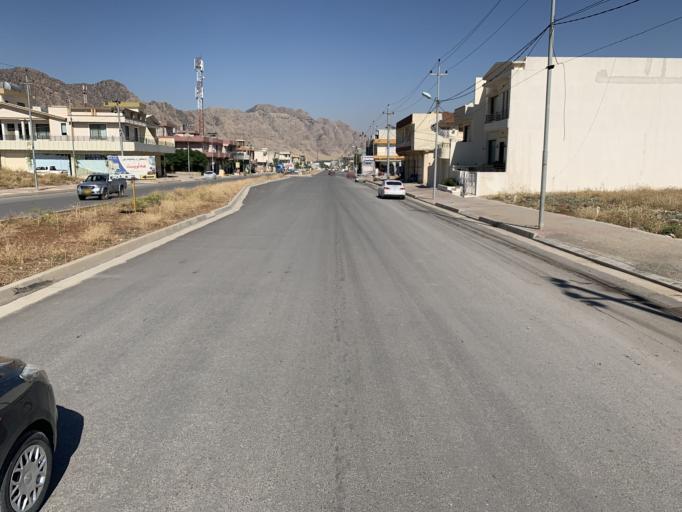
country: IQ
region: As Sulaymaniyah
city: Raniye
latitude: 36.2593
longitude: 44.8634
